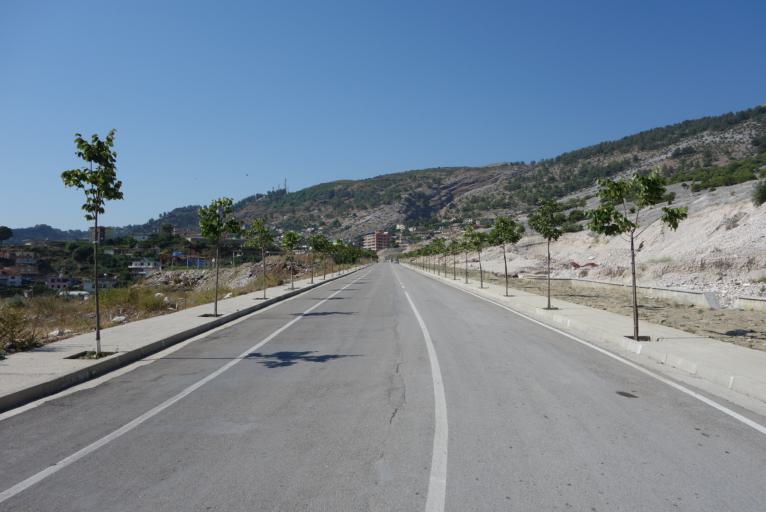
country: AL
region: Gjirokaster
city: Gjirokaster
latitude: 40.0858
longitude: 20.1313
